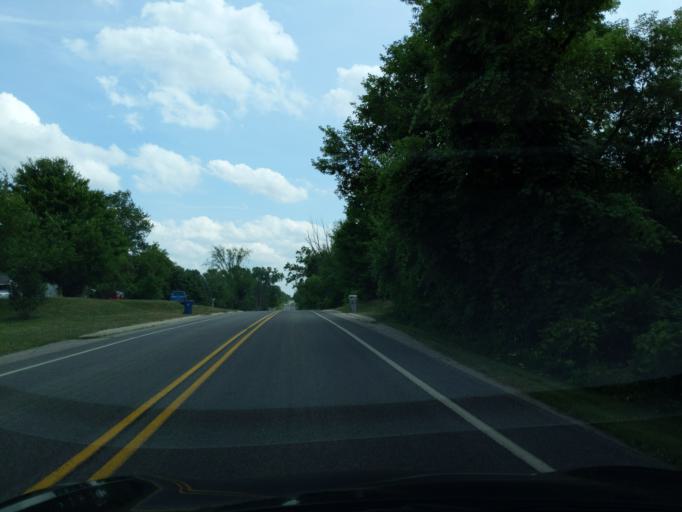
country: US
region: Michigan
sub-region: Eaton County
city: Dimondale
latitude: 42.6023
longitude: -84.6026
